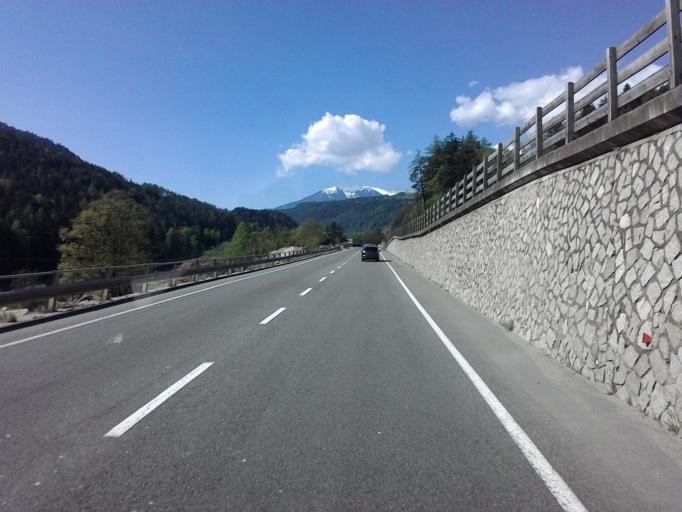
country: IT
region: Trentino-Alto Adige
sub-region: Bolzano
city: Rio di Pusteria
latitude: 46.8081
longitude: 11.6820
